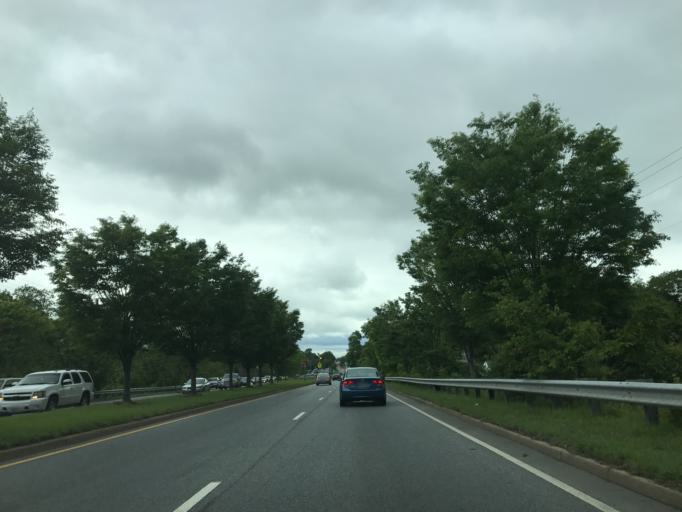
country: US
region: Maryland
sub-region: Prince George's County
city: East Riverdale
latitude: 38.9618
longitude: -76.9255
